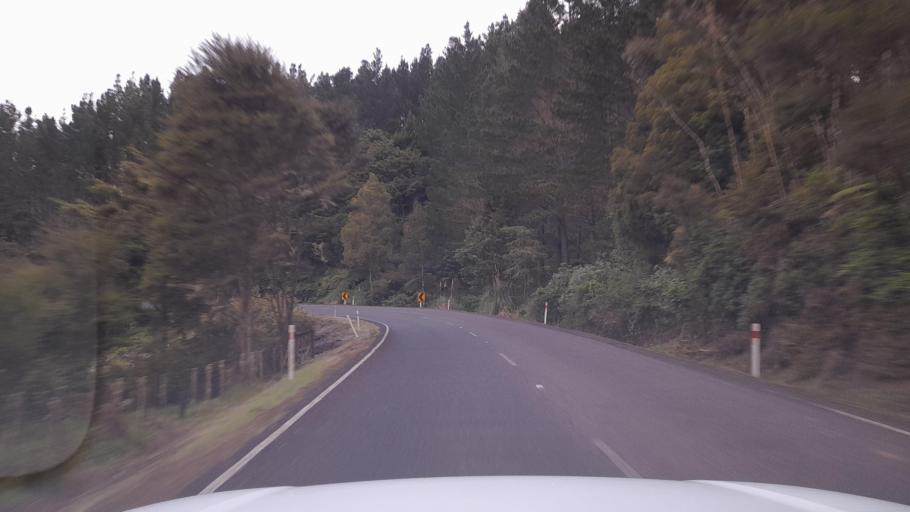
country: NZ
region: Northland
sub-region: Far North District
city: Waimate North
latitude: -35.6039
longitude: 173.8423
